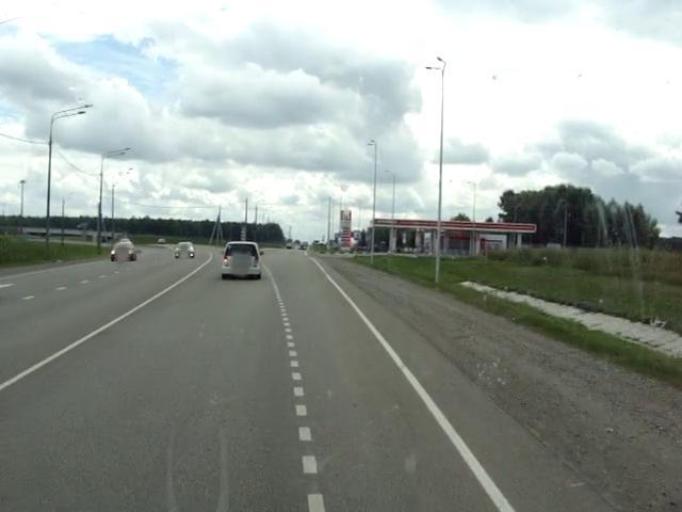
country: RU
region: Altai Krai
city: Zarya
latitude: 52.5807
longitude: 85.1756
